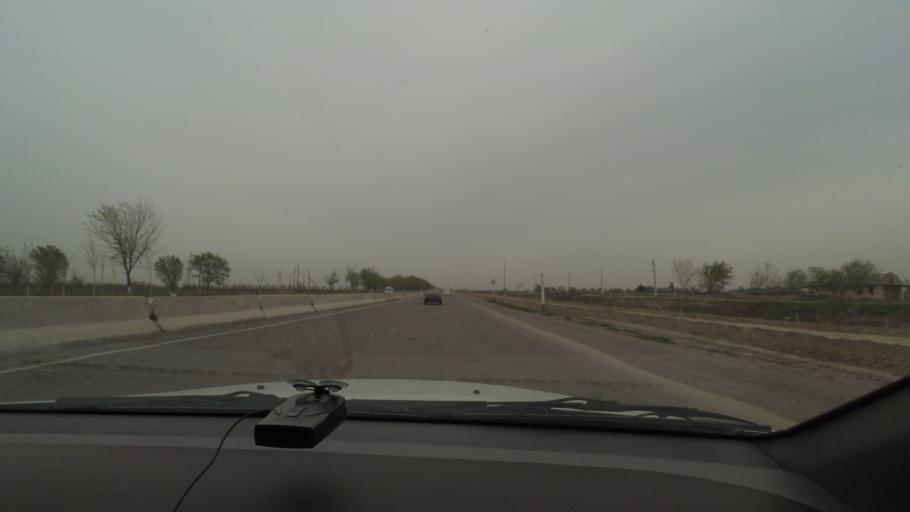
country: KZ
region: Ongtustik Qazaqstan
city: Myrzakent
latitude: 40.5346
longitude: 68.4314
